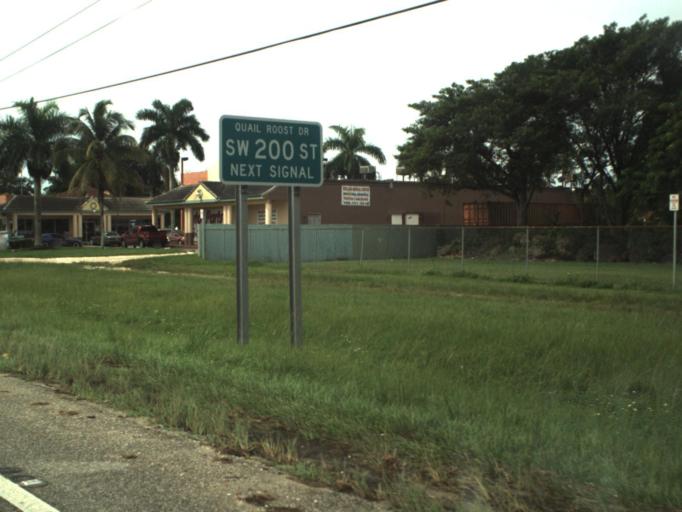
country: US
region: Florida
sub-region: Miami-Dade County
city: Richmond West
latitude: 25.5824
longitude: -80.4784
